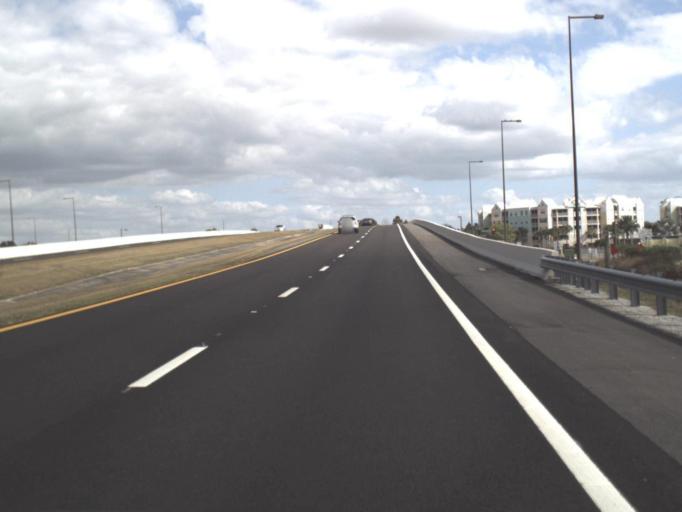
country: US
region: Florida
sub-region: Osceola County
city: Celebration
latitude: 28.3401
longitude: -81.4873
